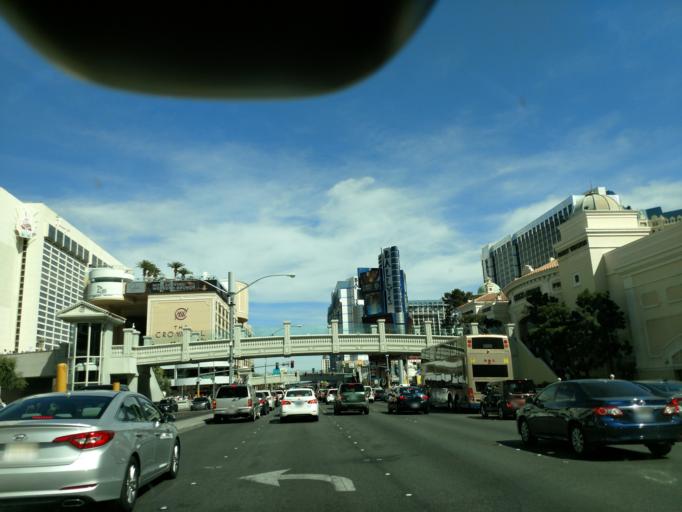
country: US
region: Nevada
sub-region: Clark County
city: Paradise
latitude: 36.1147
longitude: -115.1744
